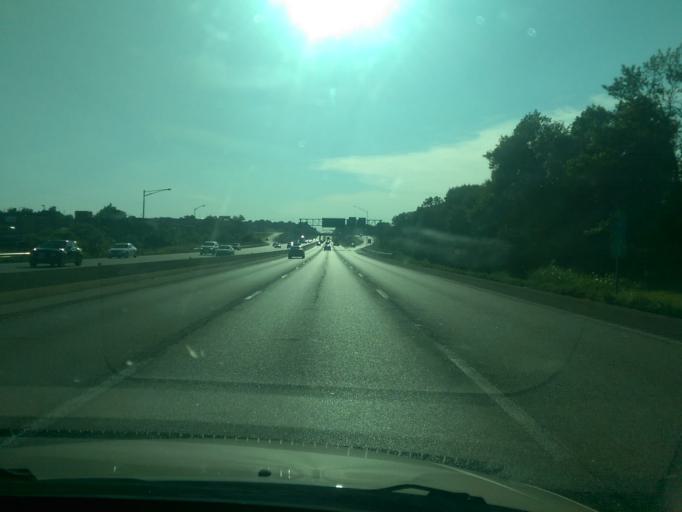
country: US
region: Missouri
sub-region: Jackson County
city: Independence
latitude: 39.0458
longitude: -94.4081
